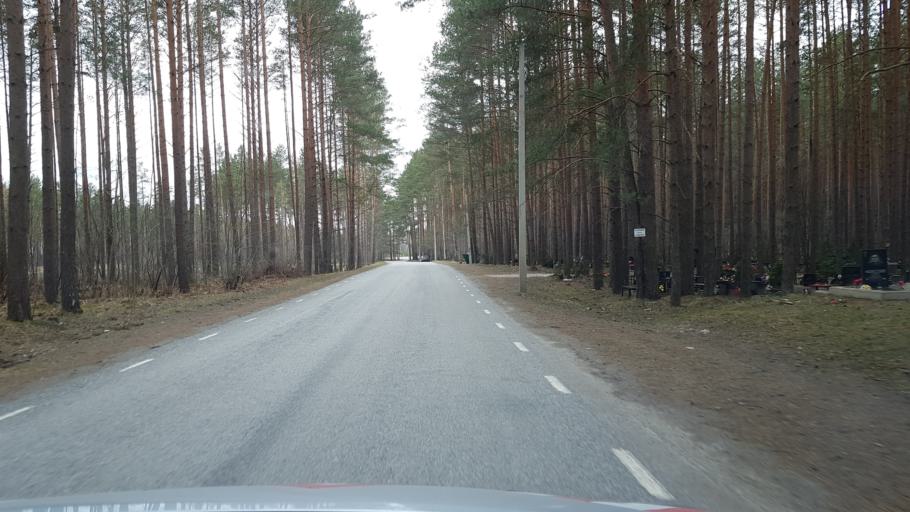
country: EE
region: Ida-Virumaa
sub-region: Narva-Joesuu linn
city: Narva-Joesuu
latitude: 59.4216
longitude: 28.1117
